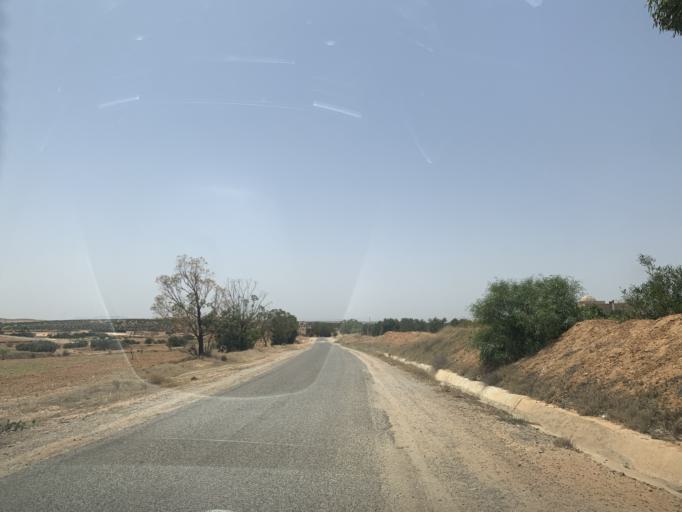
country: TN
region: Al Mahdiyah
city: Shurban
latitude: 35.1606
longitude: 10.2539
